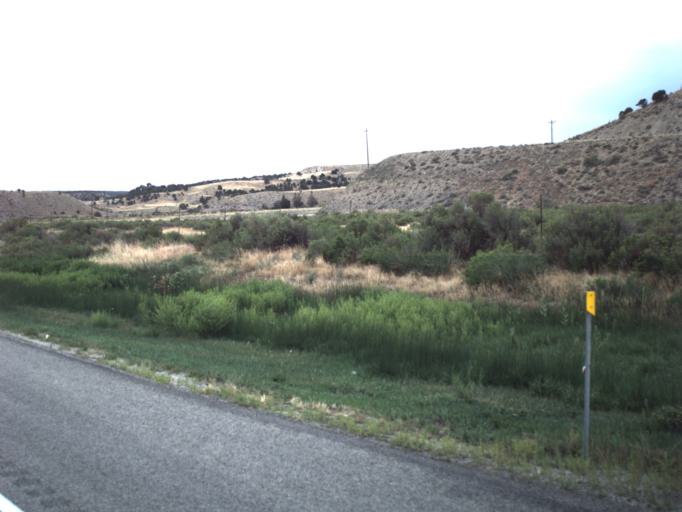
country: US
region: Utah
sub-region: Carbon County
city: Spring Glen
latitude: 39.6573
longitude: -110.8607
